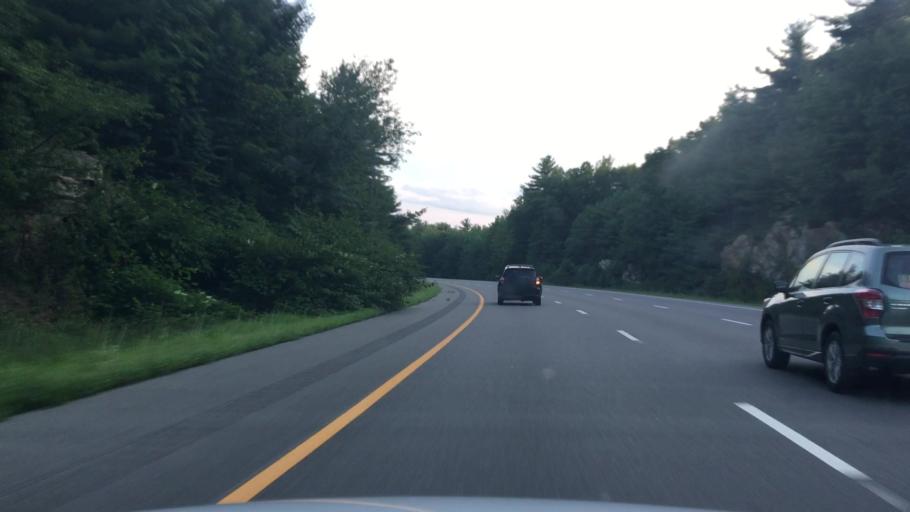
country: US
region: New Hampshire
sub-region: Merrimack County
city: Hooksett
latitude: 43.0551
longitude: -71.4742
